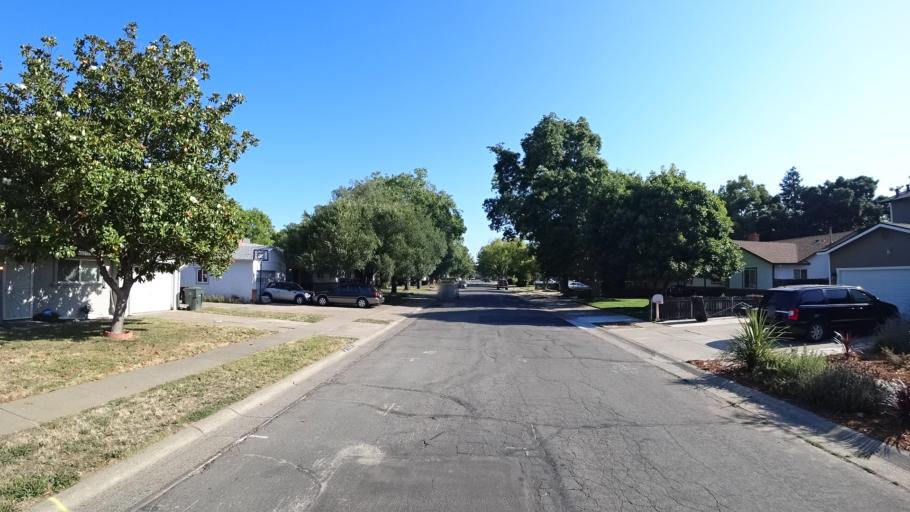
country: US
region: California
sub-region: Sacramento County
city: Florin
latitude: 38.5368
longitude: -121.4287
